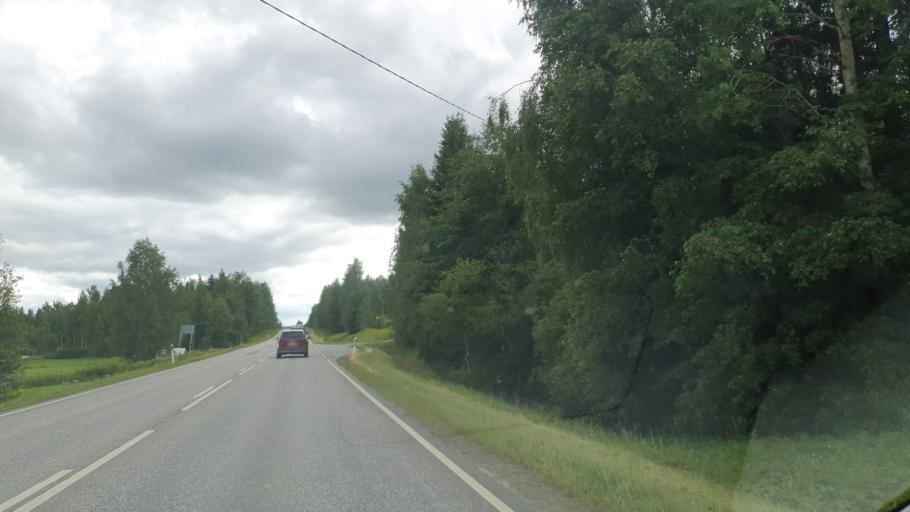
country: FI
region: Northern Savo
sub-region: Ylae-Savo
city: Sonkajaervi
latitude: 63.7205
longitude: 27.3679
